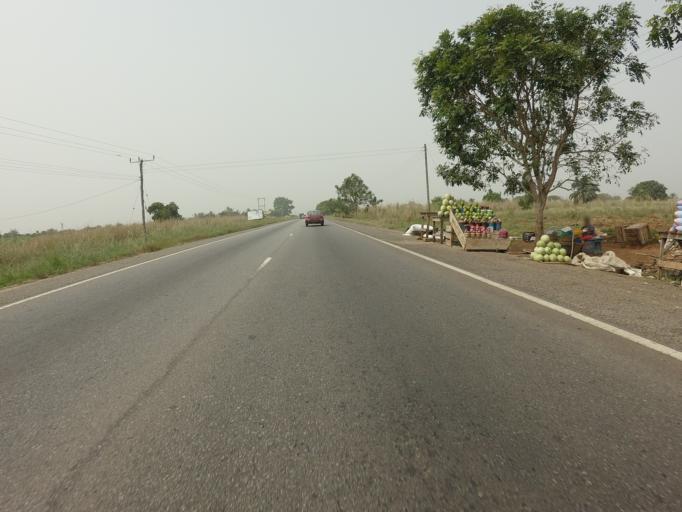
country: GH
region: Volta
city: Anloga
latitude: 5.8944
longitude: 0.5036
